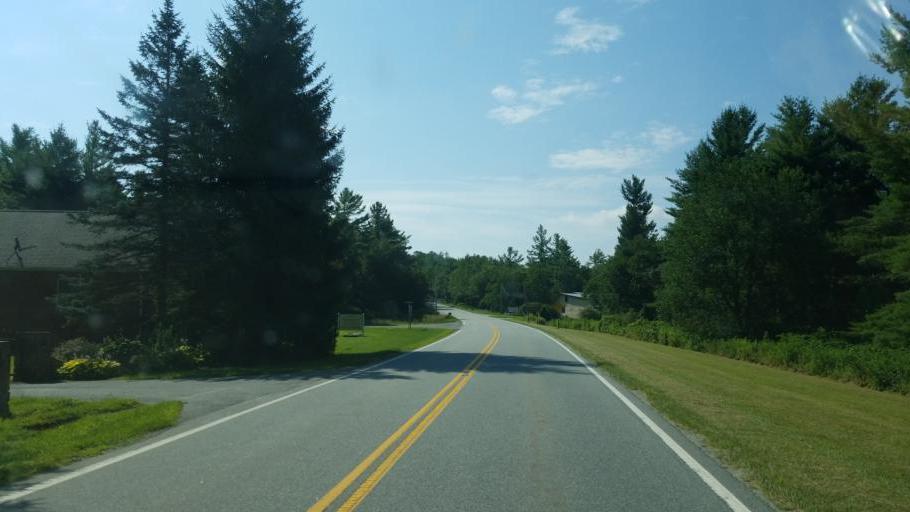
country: US
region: North Carolina
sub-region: Avery County
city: Newland
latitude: 36.0072
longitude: -81.8929
